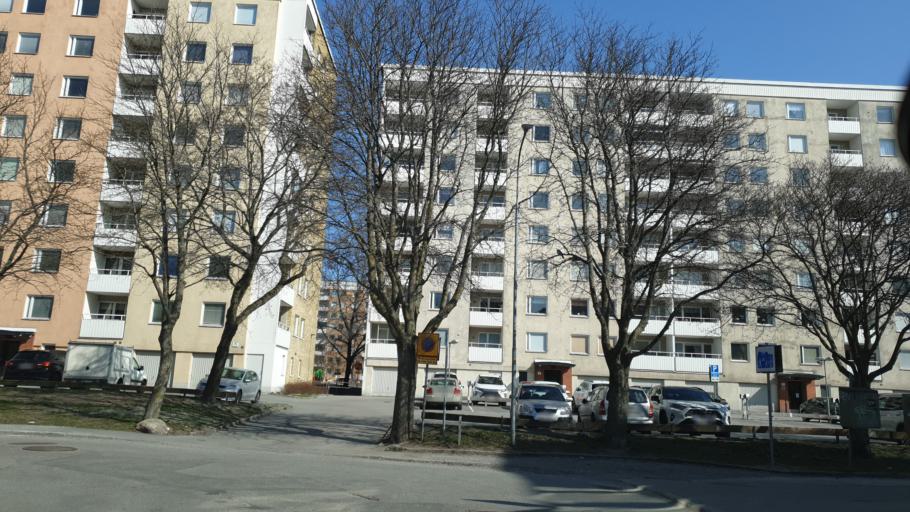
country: SE
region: Stockholm
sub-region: Jarfalla Kommun
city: Jakobsberg
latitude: 59.4243
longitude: 17.8385
